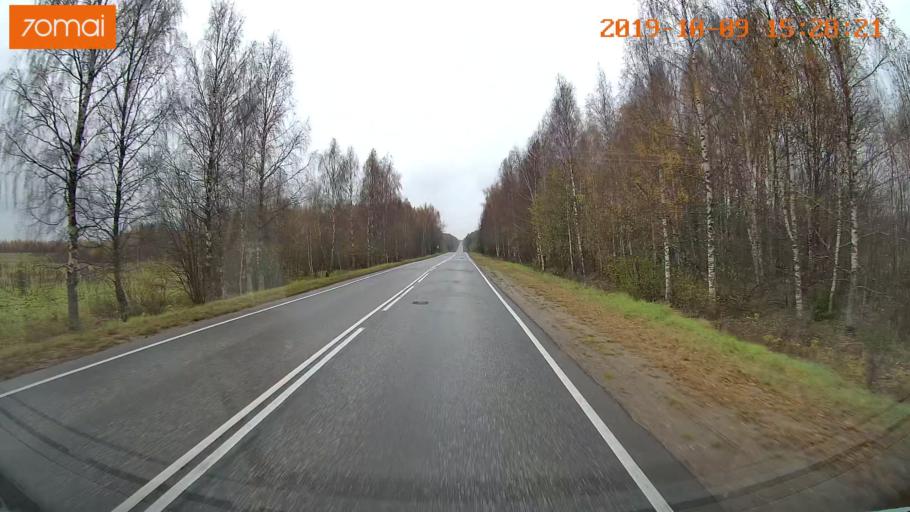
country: RU
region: Kostroma
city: Susanino
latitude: 58.0042
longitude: 41.3616
